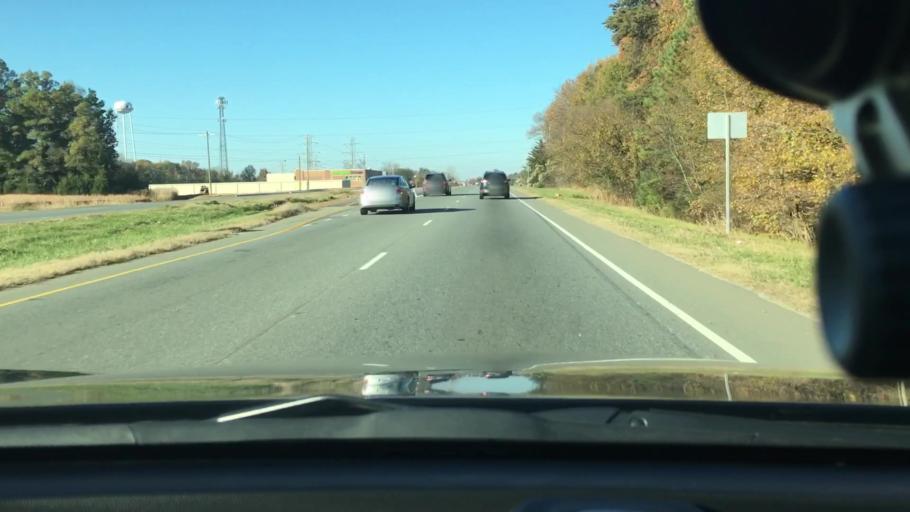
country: US
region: North Carolina
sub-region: Cabarrus County
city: Harrisburg
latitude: 35.3156
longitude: -80.6855
